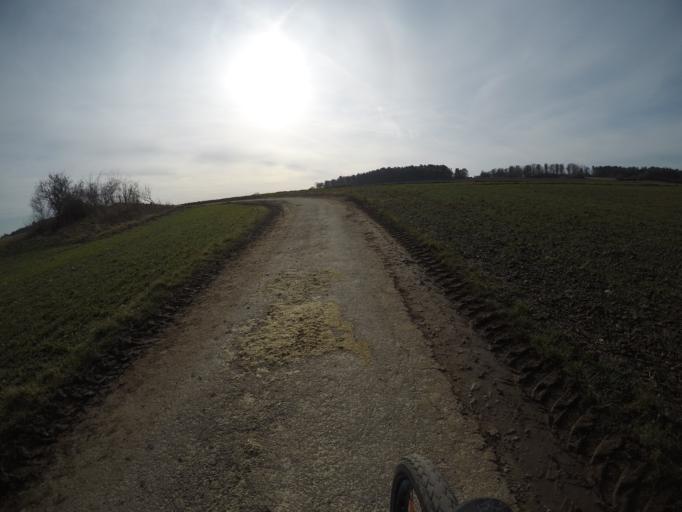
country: DE
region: Baden-Wuerttemberg
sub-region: Karlsruhe Region
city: Ostelsheim
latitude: 48.7014
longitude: 8.8663
